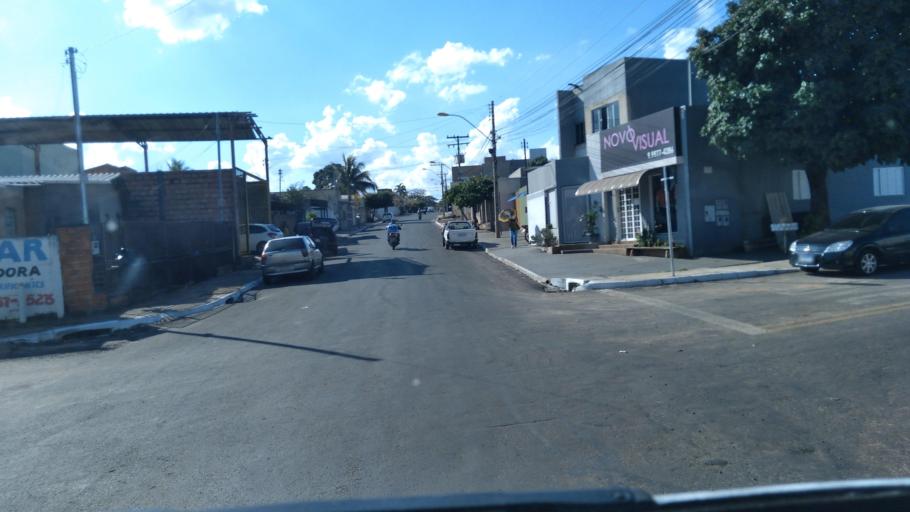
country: BR
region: Goias
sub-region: Mineiros
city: Mineiros
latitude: -17.5584
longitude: -52.5501
